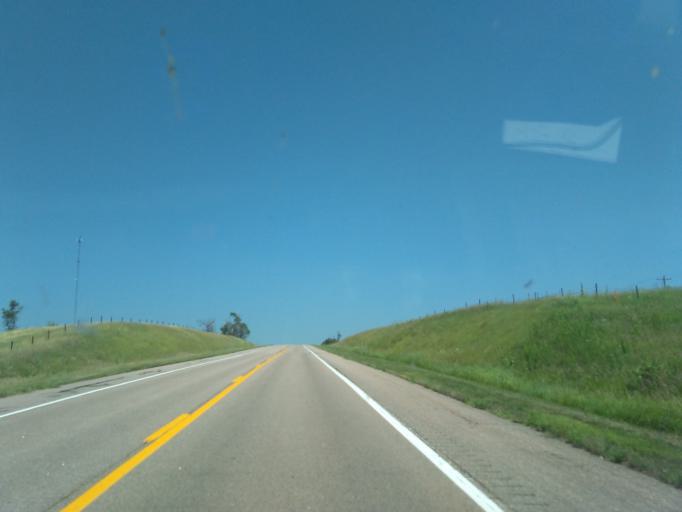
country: US
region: Nebraska
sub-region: Frontier County
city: Stockville
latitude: 40.5952
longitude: -100.6295
